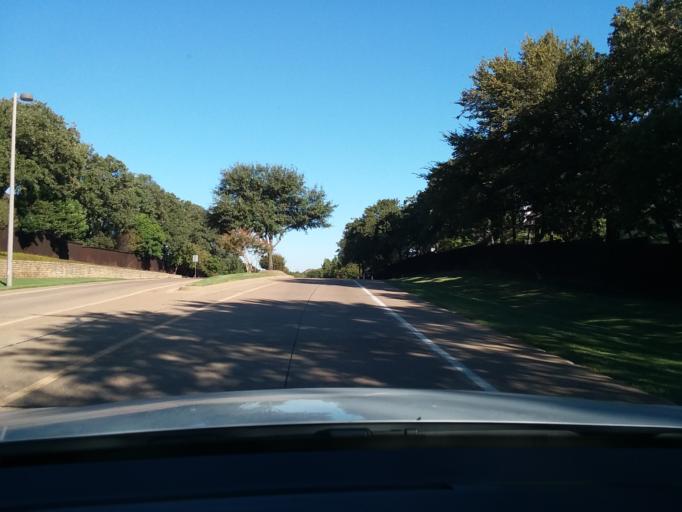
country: US
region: Texas
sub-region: Denton County
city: Highland Village
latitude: 33.0874
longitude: -97.0680
